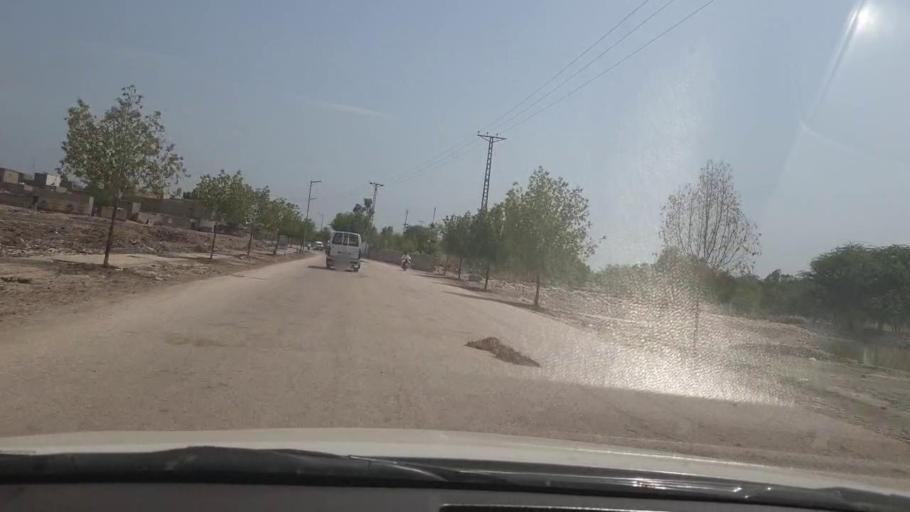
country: PK
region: Sindh
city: Garhi Yasin
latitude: 27.9067
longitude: 68.5065
